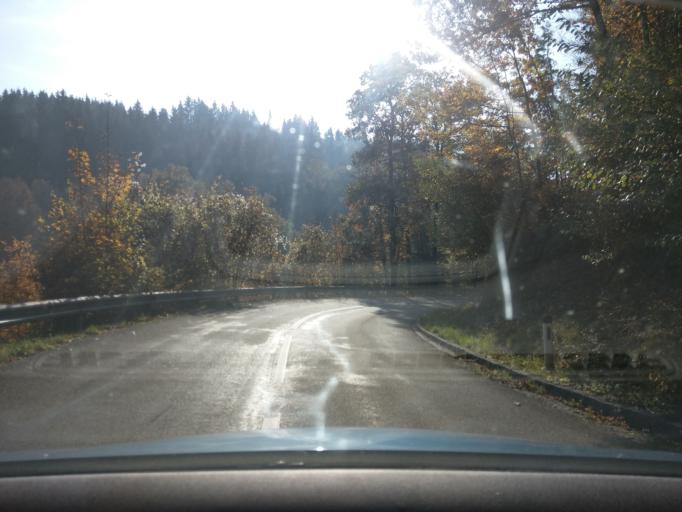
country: DE
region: Bavaria
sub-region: Lower Bavaria
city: Salzweg
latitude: 48.5667
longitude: 13.4975
